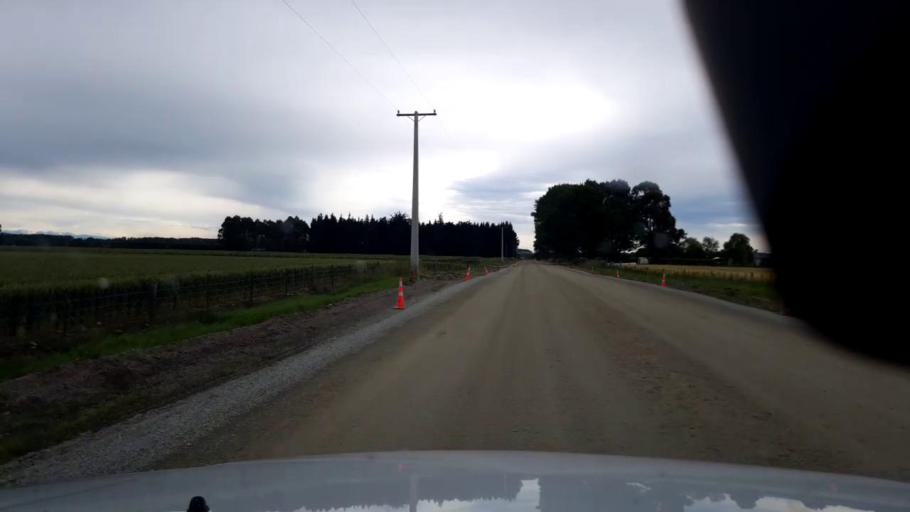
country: NZ
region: Canterbury
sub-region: Timaru District
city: Pleasant Point
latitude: -44.2788
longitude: 171.2478
